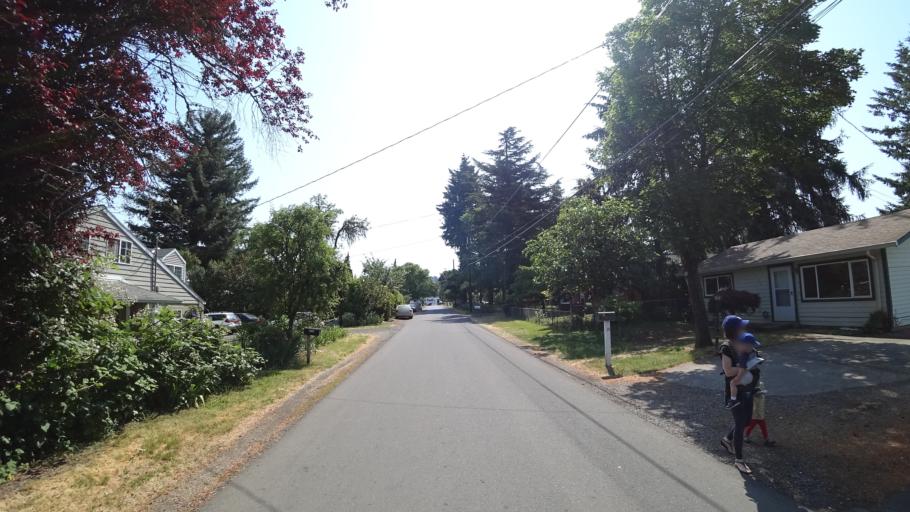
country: US
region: Oregon
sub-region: Clackamas County
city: Oatfield
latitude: 45.4512
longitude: -122.5970
